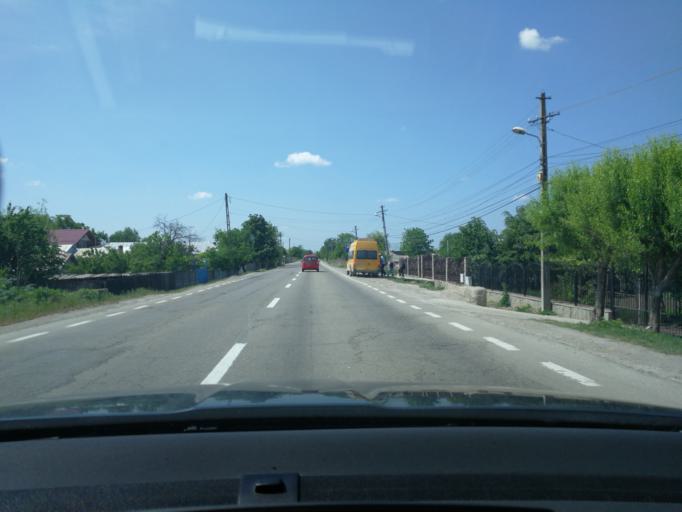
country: RO
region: Prahova
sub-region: Comuna Targsoru Vechi
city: Targsoru Vechi
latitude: 44.8744
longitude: 25.9394
